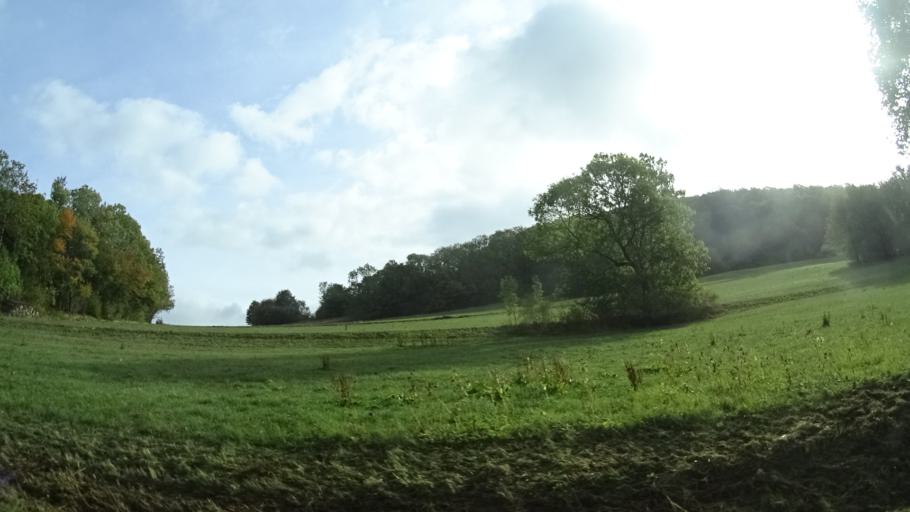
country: DE
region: Hesse
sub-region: Regierungsbezirk Kassel
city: Hilders
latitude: 50.5807
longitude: 10.0148
